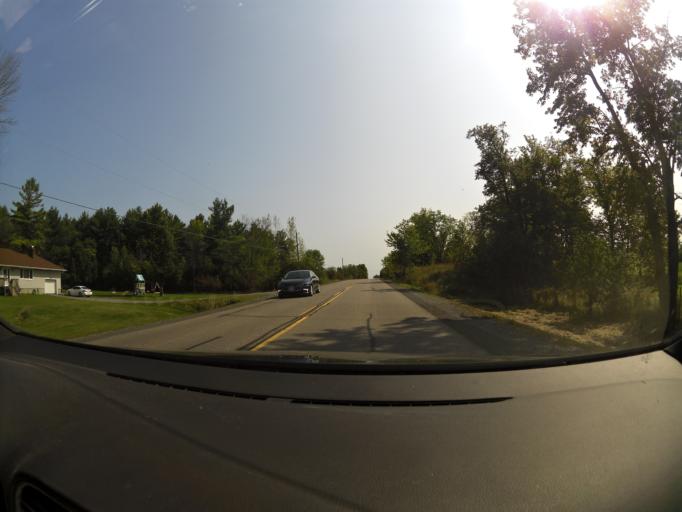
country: CA
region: Ontario
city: Arnprior
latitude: 45.4258
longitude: -76.1617
